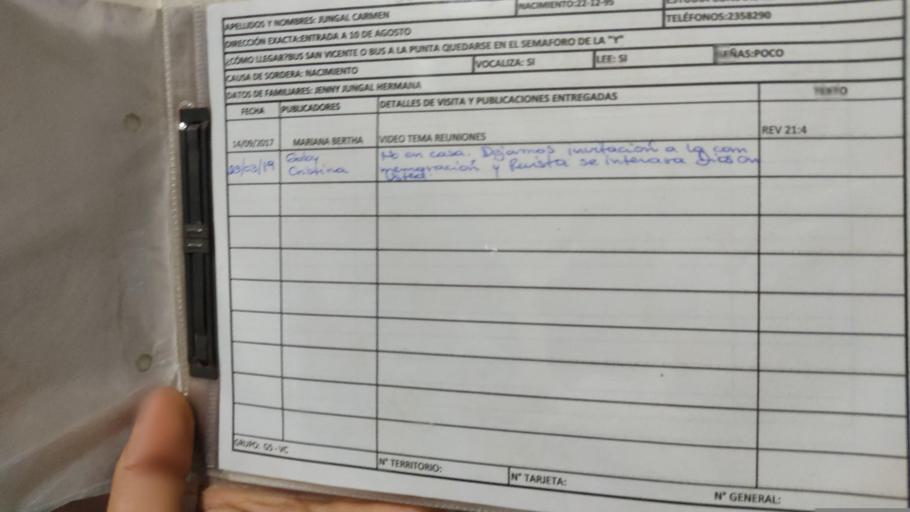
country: EC
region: Sucumbios
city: Nueva Loja
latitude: 0.0791
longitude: -76.9082
